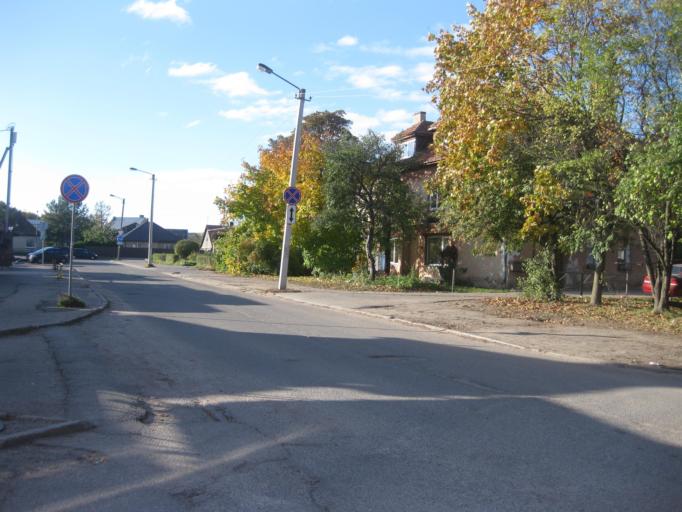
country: LT
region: Kauno apskritis
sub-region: Kaunas
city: Aleksotas
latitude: 54.8835
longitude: 23.8964
